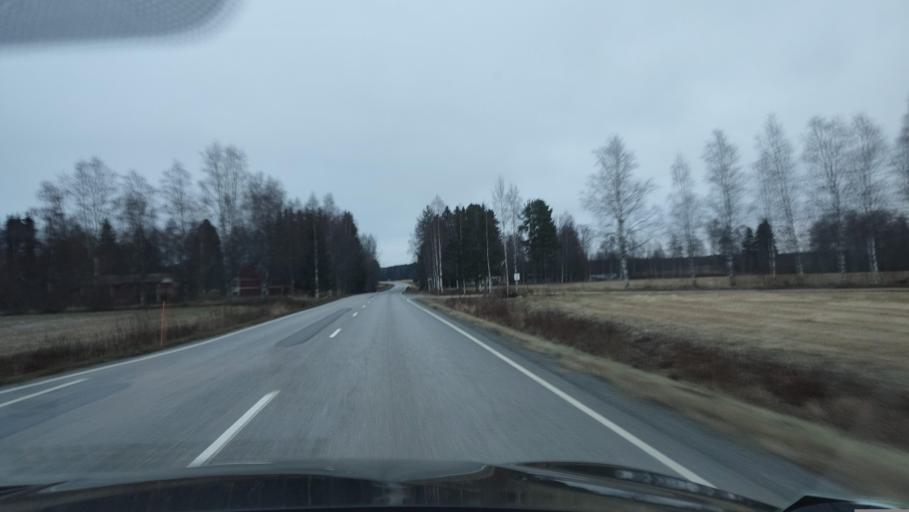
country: FI
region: Southern Ostrobothnia
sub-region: Suupohja
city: Kauhajoki
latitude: 62.3468
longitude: 22.0344
